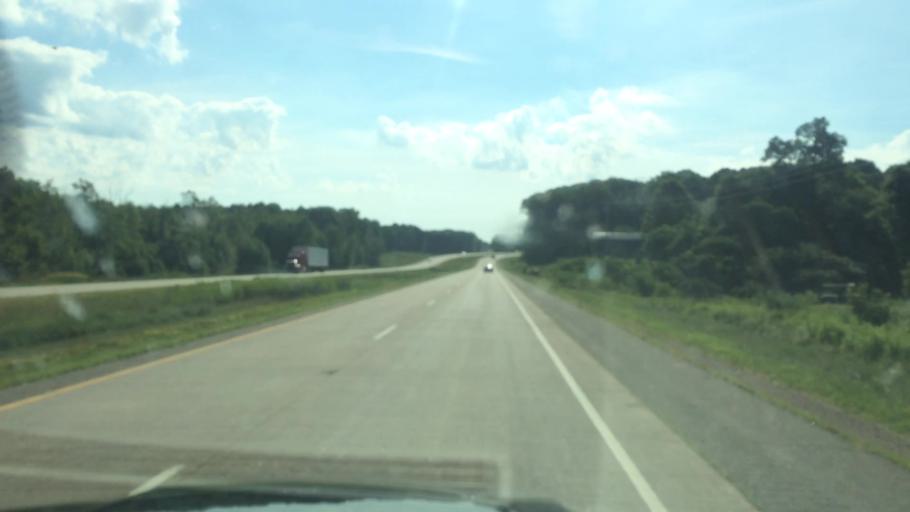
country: US
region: Wisconsin
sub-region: Shawano County
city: Wittenberg
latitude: 44.8259
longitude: -89.0764
